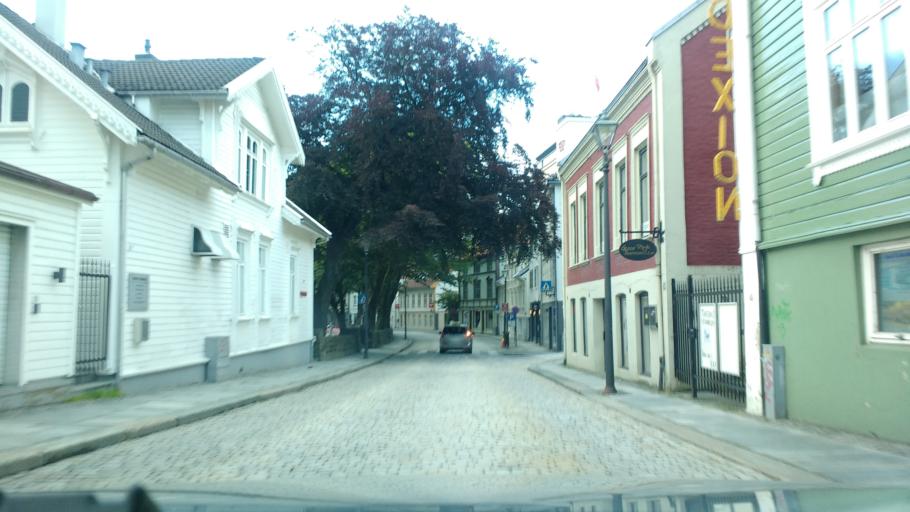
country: NO
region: Rogaland
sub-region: Stavanger
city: Stavanger
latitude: 58.9678
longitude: 5.7349
